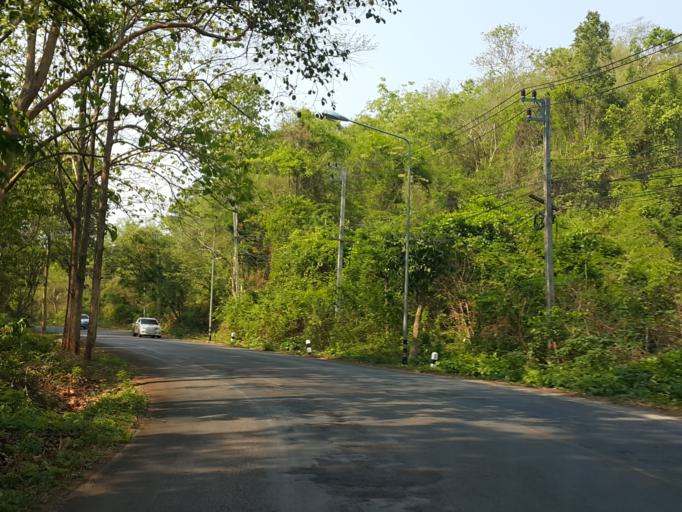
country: TH
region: Kanchanaburi
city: Sai Yok
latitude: 14.1228
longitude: 99.1544
